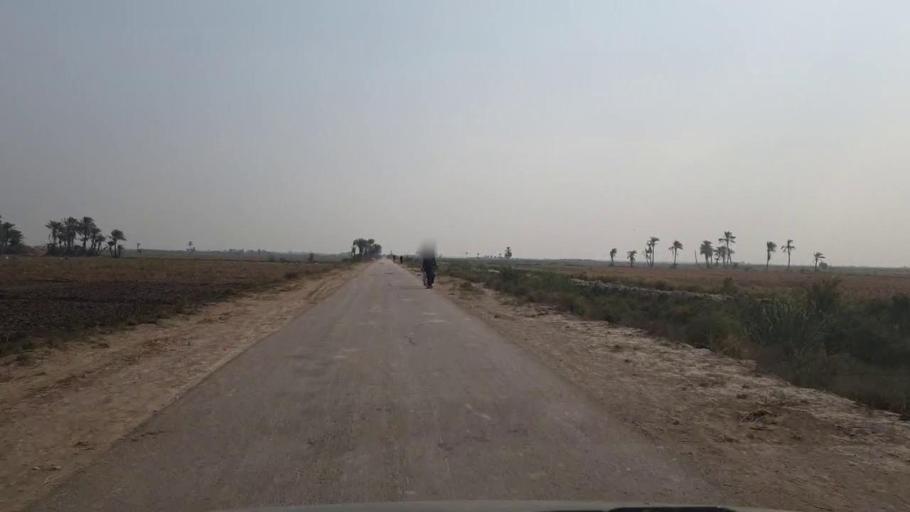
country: PK
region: Sindh
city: Tando Muhammad Khan
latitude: 25.1034
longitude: 68.3716
